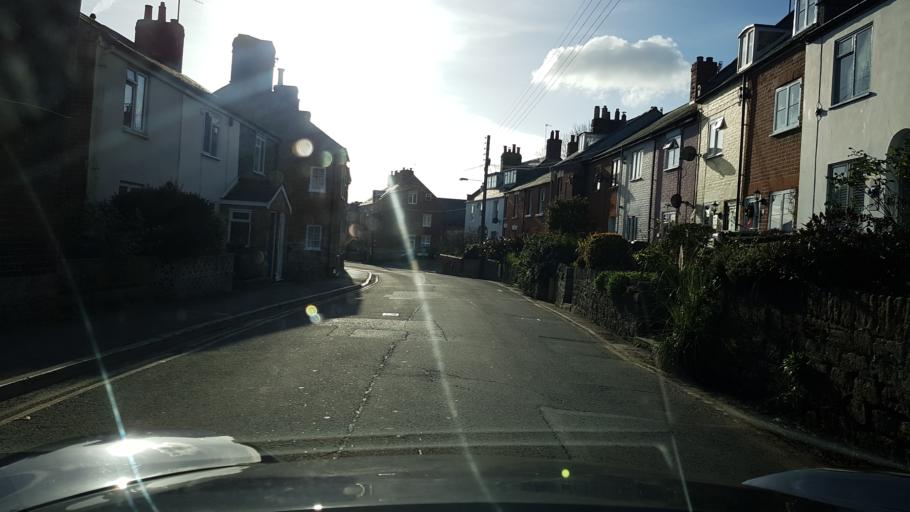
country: GB
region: England
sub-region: Dorset
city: Bridport
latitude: 50.7367
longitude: -2.7645
